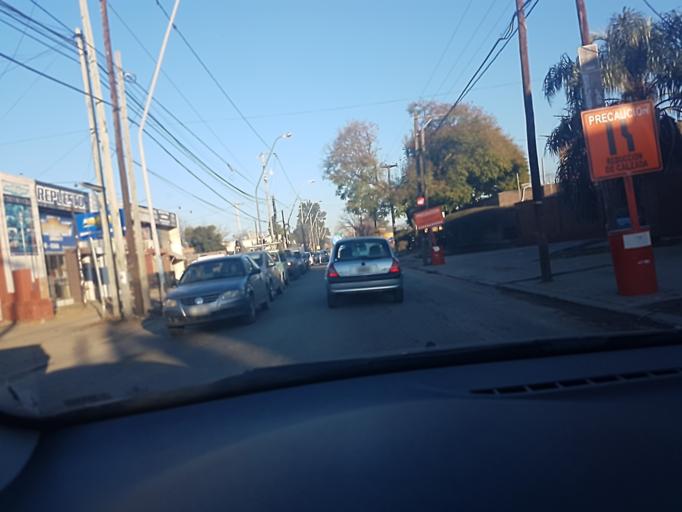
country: AR
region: Cordoba
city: Villa Allende
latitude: -31.3433
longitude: -64.2437
